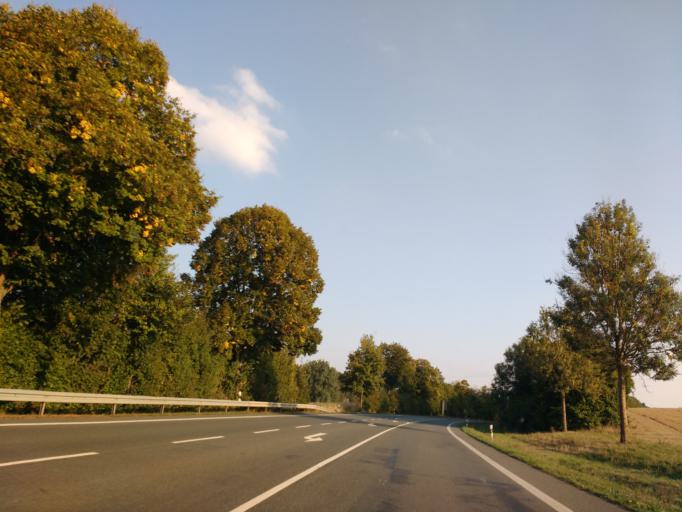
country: DE
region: North Rhine-Westphalia
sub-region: Regierungsbezirk Detmold
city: Willebadessen
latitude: 51.6280
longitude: 9.1367
